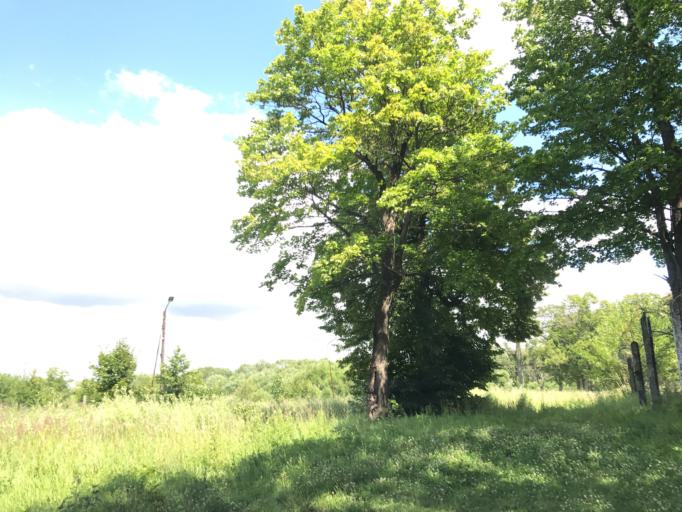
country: RU
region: Kaliningrad
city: Bol'shoe Isakovo
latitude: 54.6578
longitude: 20.5663
